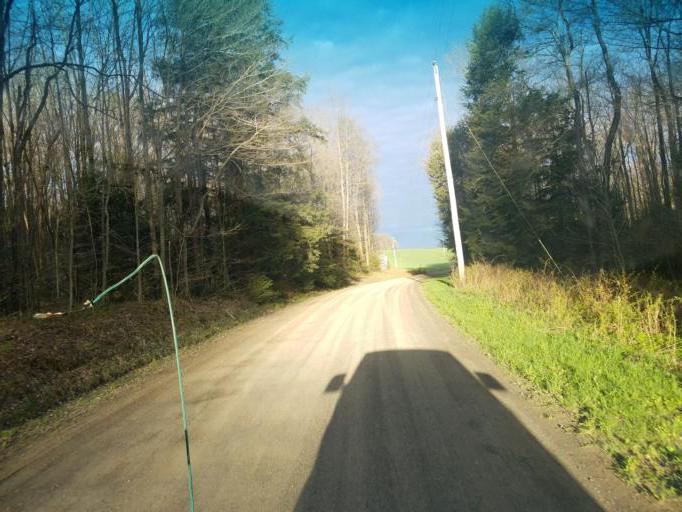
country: US
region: Pennsylvania
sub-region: Potter County
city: Galeton
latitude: 41.9020
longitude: -77.7304
